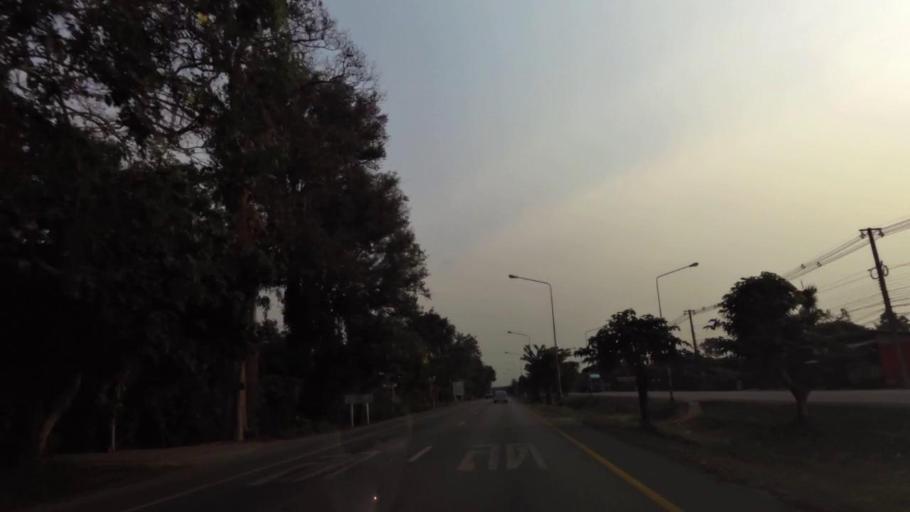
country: TH
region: Chanthaburi
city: Khlung
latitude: 12.5053
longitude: 102.1700
